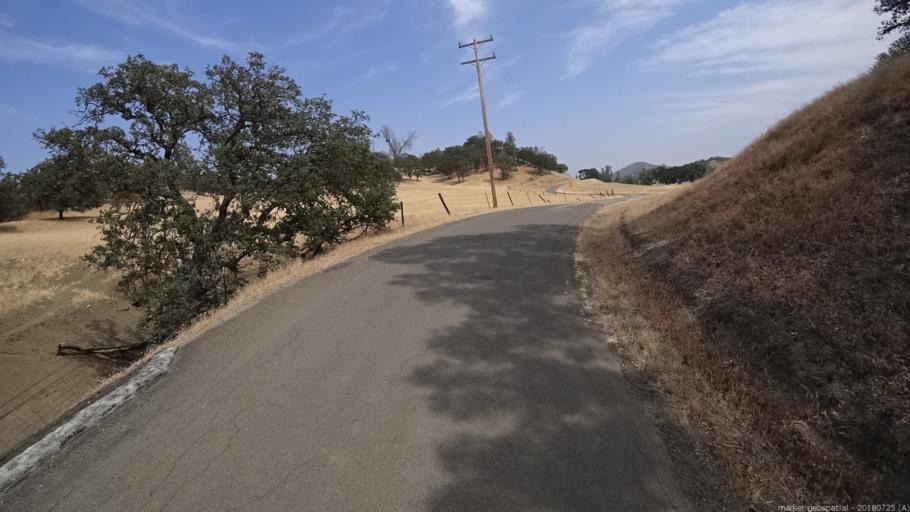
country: US
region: California
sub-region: Fresno County
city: Coalinga
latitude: 36.1837
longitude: -120.6872
